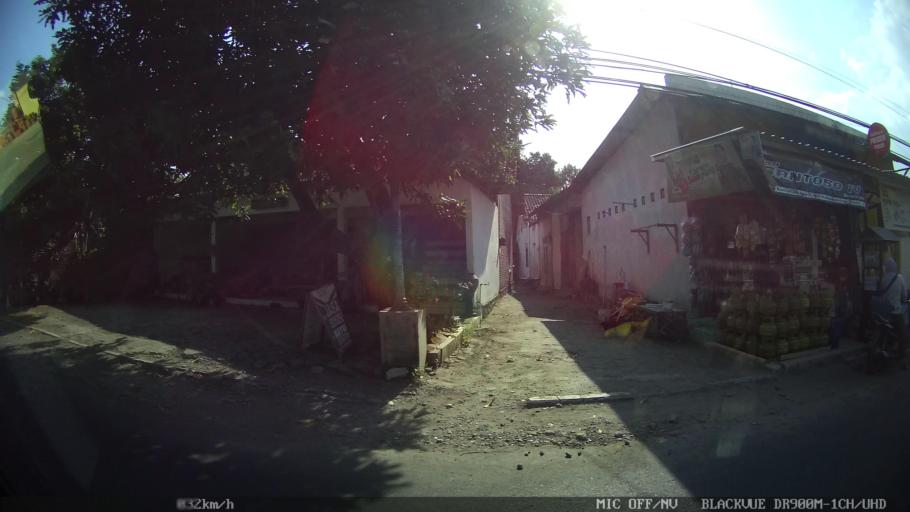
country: ID
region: Daerah Istimewa Yogyakarta
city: Kasihan
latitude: -7.8444
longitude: 110.3350
